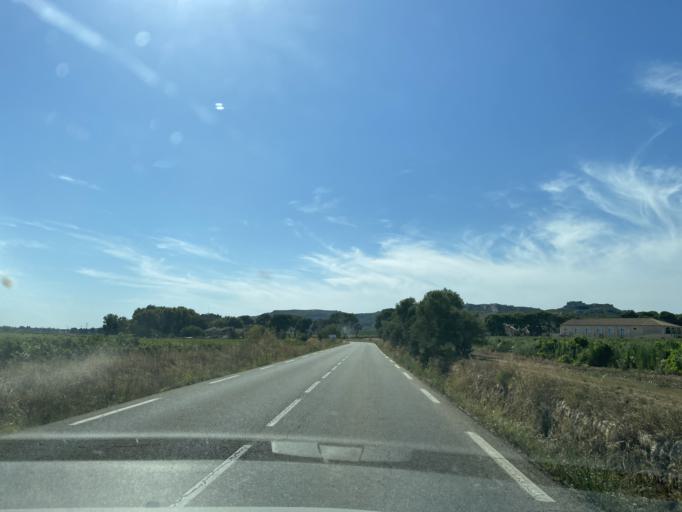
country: FR
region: Provence-Alpes-Cote d'Azur
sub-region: Departement des Bouches-du-Rhone
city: La Fare-les-Oliviers
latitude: 43.5475
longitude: 5.1590
